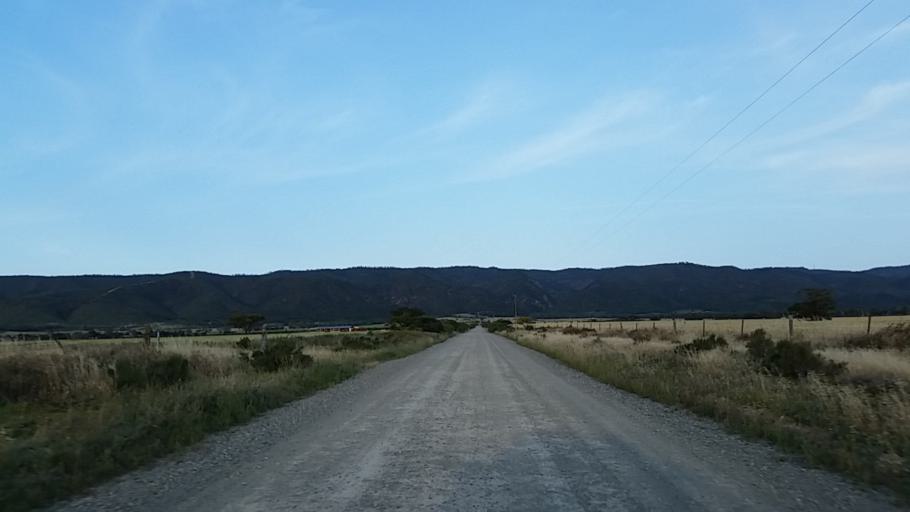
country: AU
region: South Australia
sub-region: Port Pirie City and Dists
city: Port Pirie
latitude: -33.0548
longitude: 138.0840
